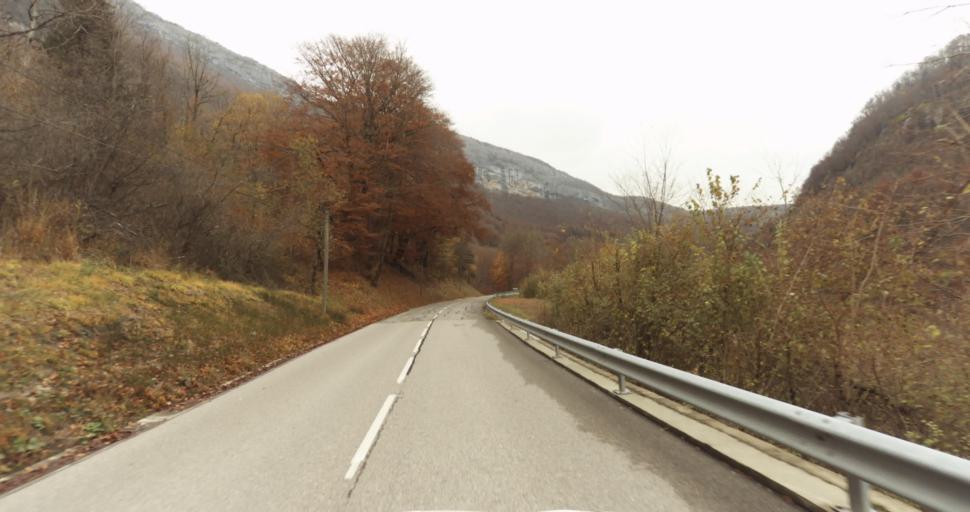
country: FR
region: Rhone-Alpes
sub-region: Departement de la Haute-Savoie
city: Gruffy
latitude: 45.7481
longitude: 6.0899
